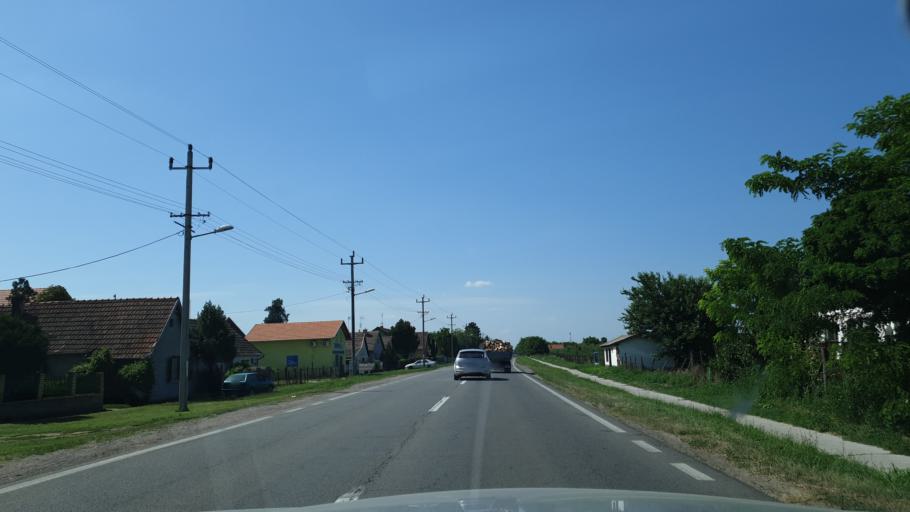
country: HU
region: Bacs-Kiskun
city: Kelebia
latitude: 46.1395
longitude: 19.5918
